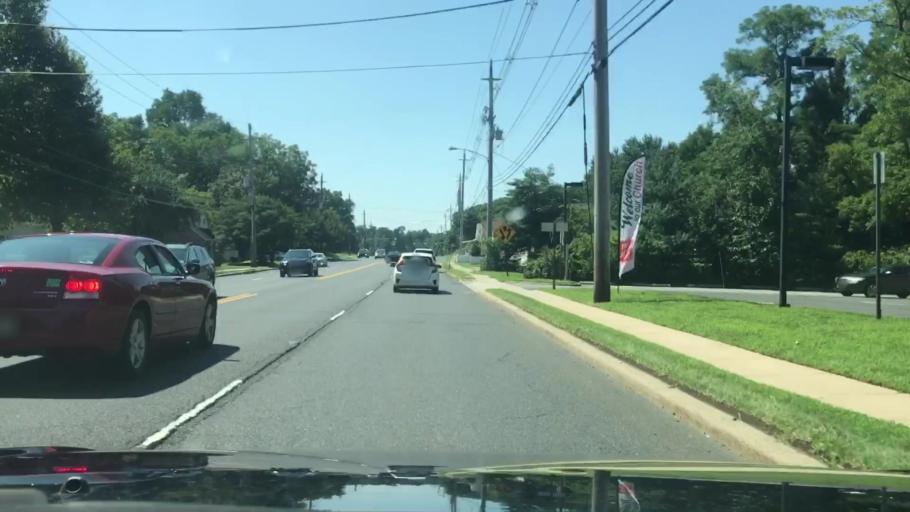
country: US
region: New Jersey
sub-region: Monmouth County
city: Red Bank
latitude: 40.3367
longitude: -74.0825
